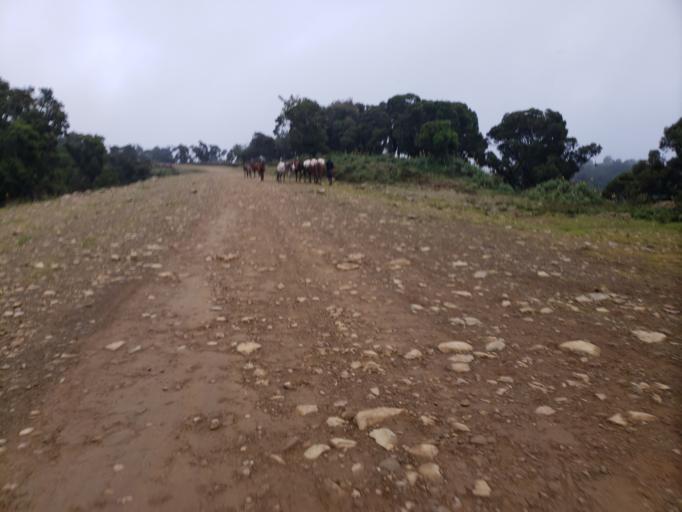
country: ET
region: Oromiya
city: Dodola
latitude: 6.7256
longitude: 39.4241
